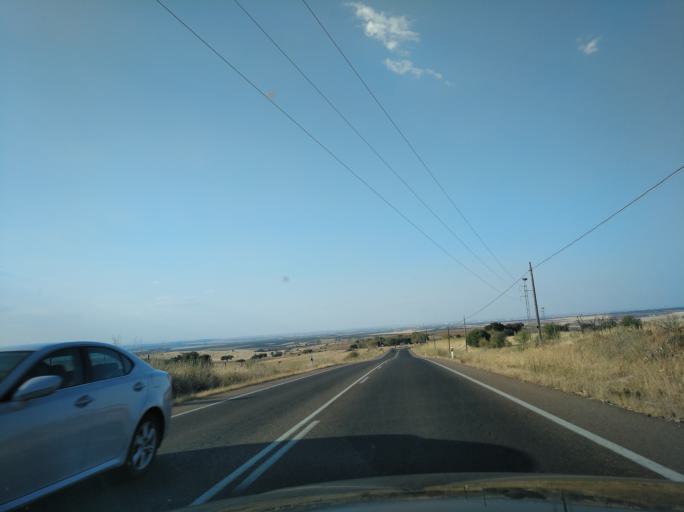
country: ES
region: Extremadura
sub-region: Provincia de Badajoz
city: Olivenza
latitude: 38.7152
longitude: -7.0848
